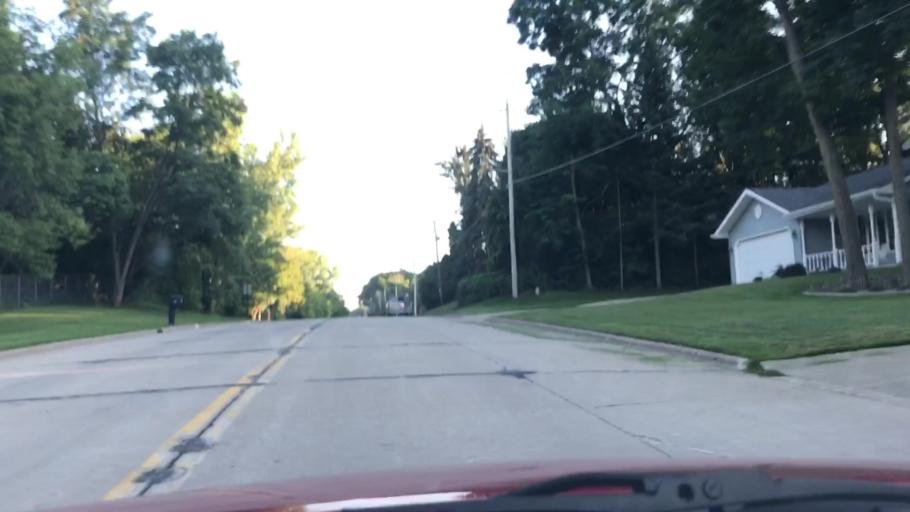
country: US
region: Wisconsin
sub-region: Brown County
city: Howard
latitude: 44.5306
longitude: -88.1097
